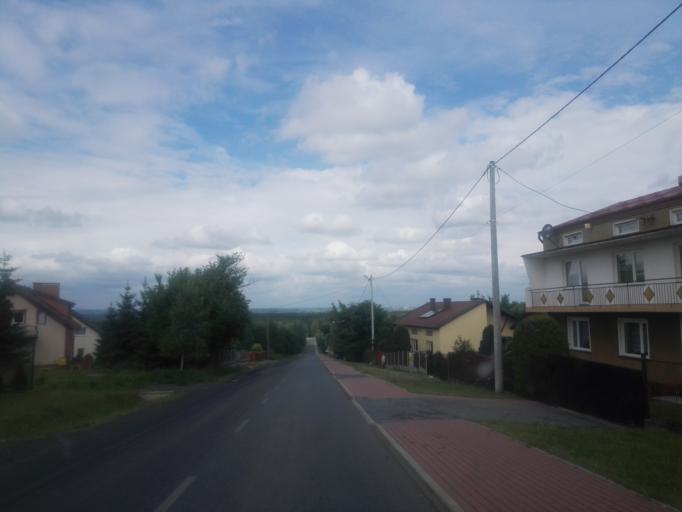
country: PL
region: Silesian Voivodeship
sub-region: Powiat myszkowski
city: Choron
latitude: 50.7113
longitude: 19.2678
